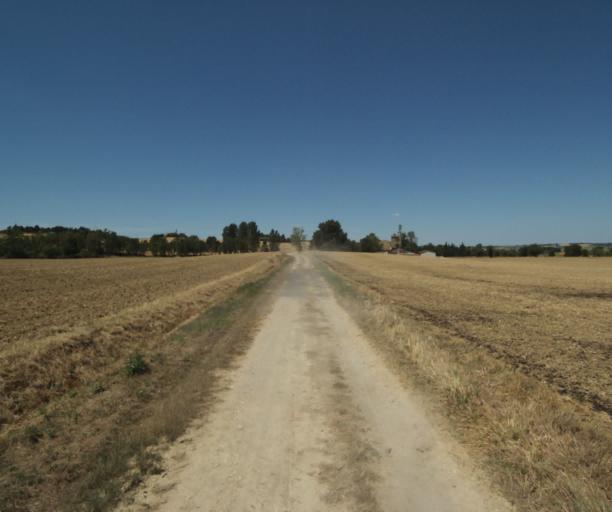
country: FR
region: Midi-Pyrenees
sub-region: Departement de la Haute-Garonne
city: Saint-Felix-Lauragais
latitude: 43.4535
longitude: 1.8992
